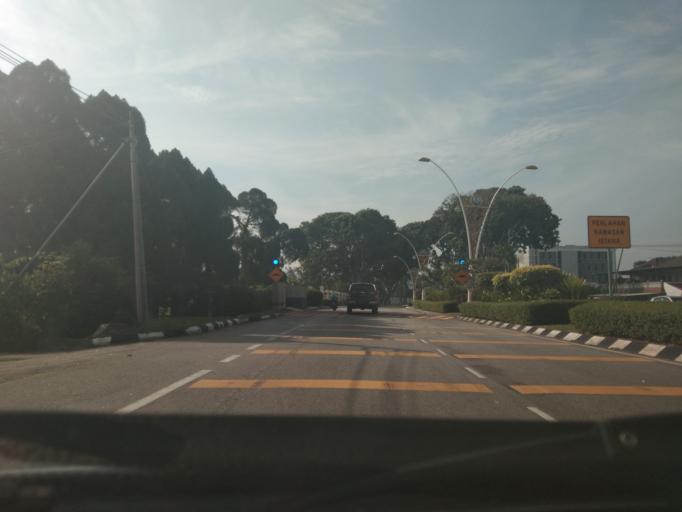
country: MY
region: Perak
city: Ipoh
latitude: 4.5875
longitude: 101.0977
